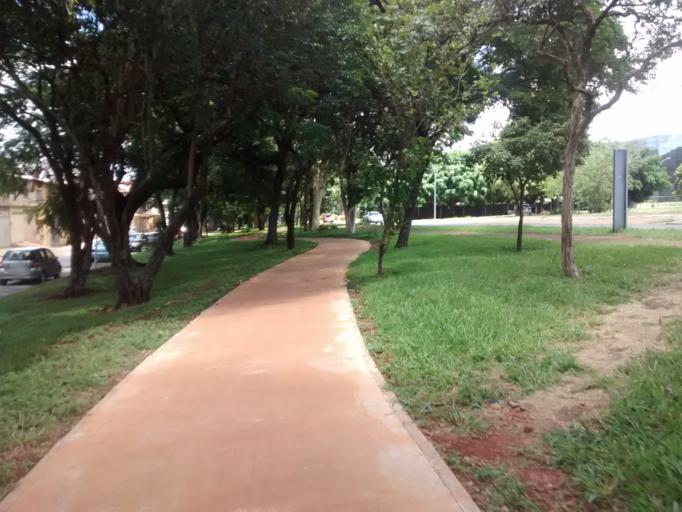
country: BR
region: Federal District
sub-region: Brasilia
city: Brasilia
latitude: -15.8083
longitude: -47.9049
